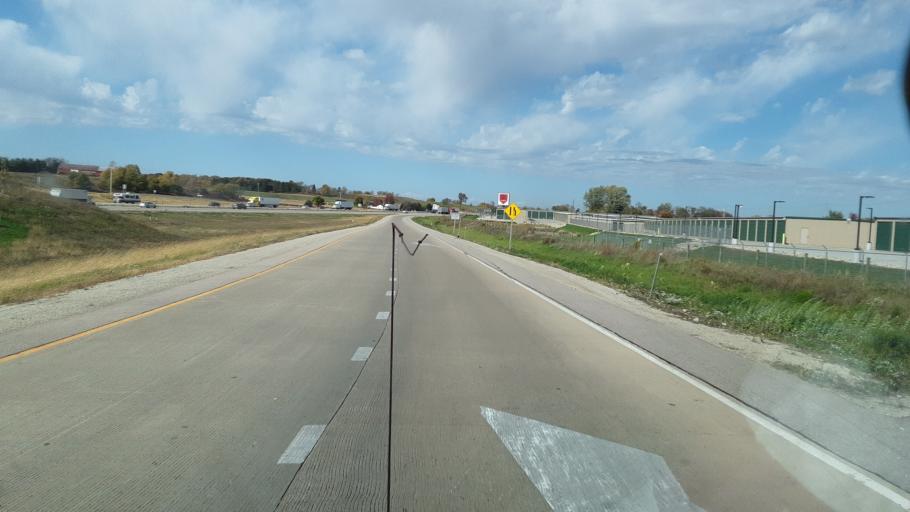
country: US
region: Wisconsin
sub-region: Rock County
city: Edgerton
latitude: 42.8365
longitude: -89.0268
